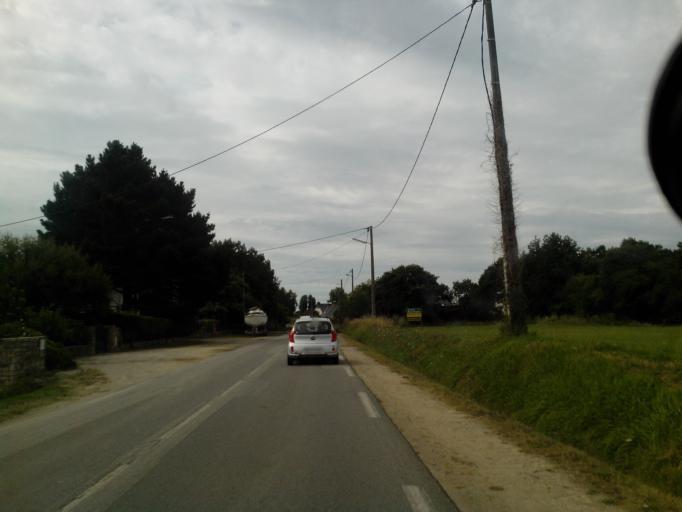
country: FR
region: Brittany
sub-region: Departement du Morbihan
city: Erdeven
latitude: 47.6374
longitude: -3.1562
